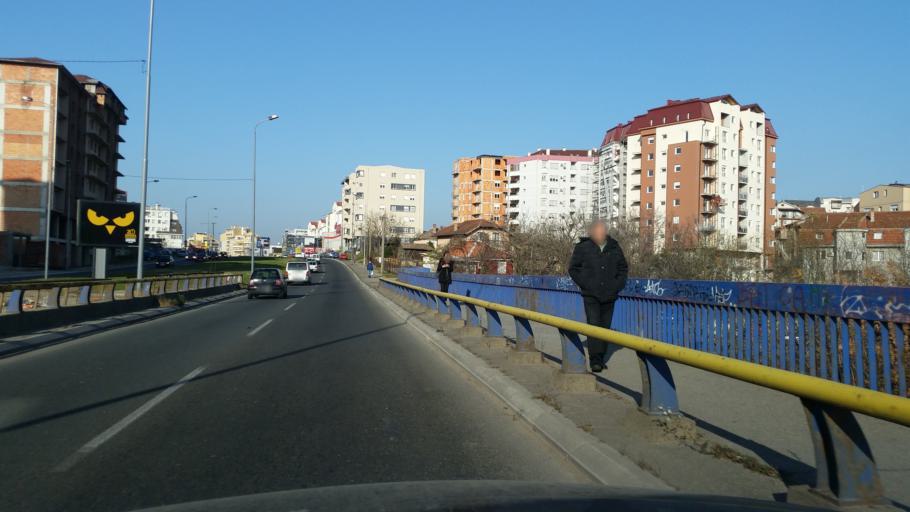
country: RS
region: Central Serbia
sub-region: Belgrade
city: Cukarica
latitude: 44.7564
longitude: 20.4153
